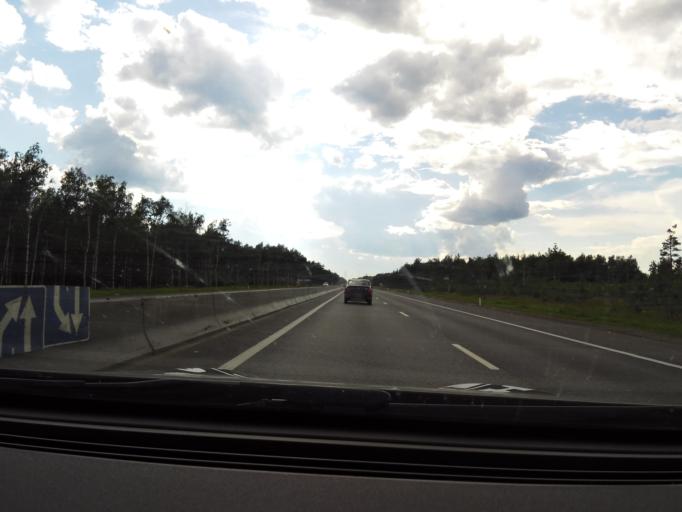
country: RU
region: Nizjnij Novgorod
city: Dzerzhinsk
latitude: 56.2990
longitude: 43.4910
